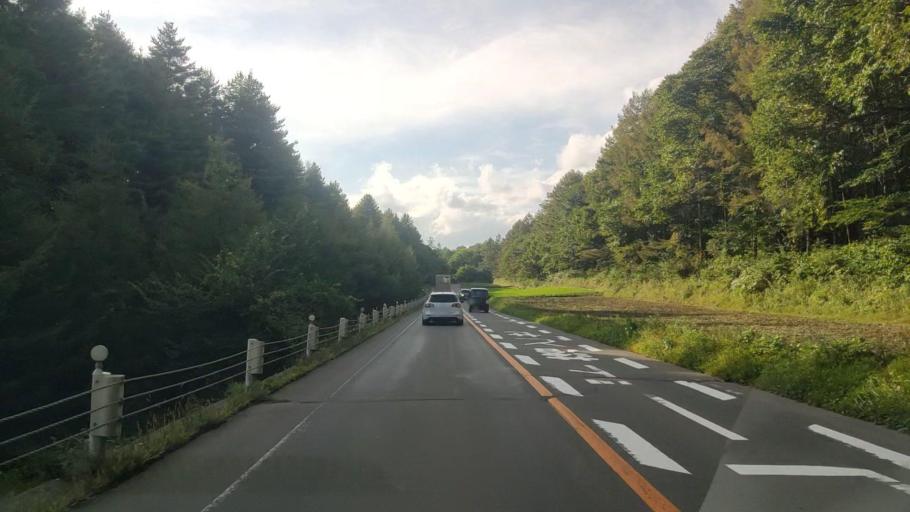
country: JP
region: Nagano
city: Ueda
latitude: 36.4859
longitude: 138.4263
